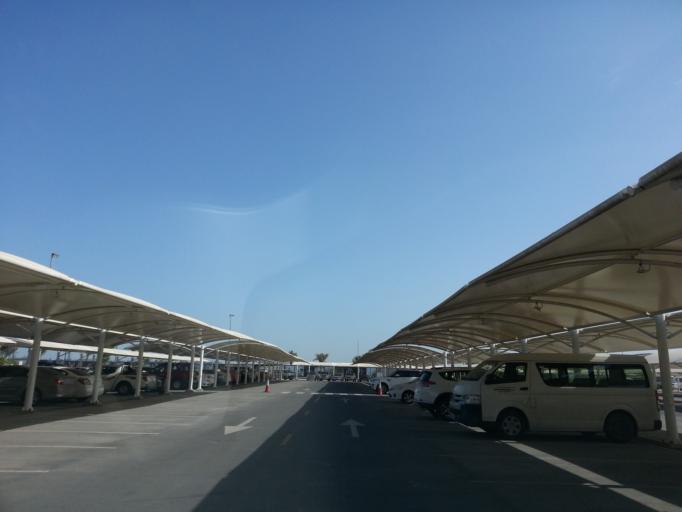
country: AE
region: Dubai
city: Dubai
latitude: 25.1881
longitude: 55.2988
